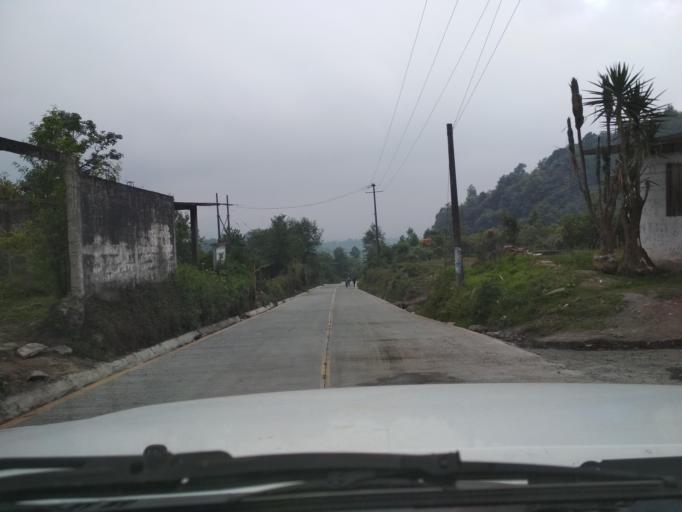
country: MX
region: Veracruz
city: La Perla
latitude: 18.9303
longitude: -97.1398
